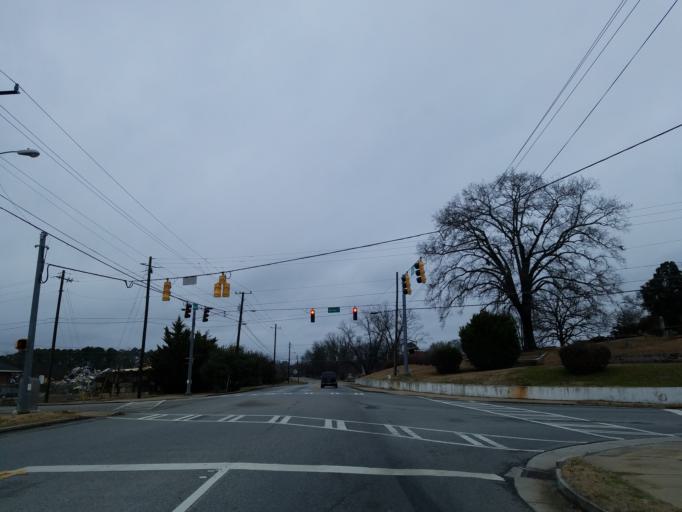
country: US
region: Georgia
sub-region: Bartow County
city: Cartersville
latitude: 34.1751
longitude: -84.8103
